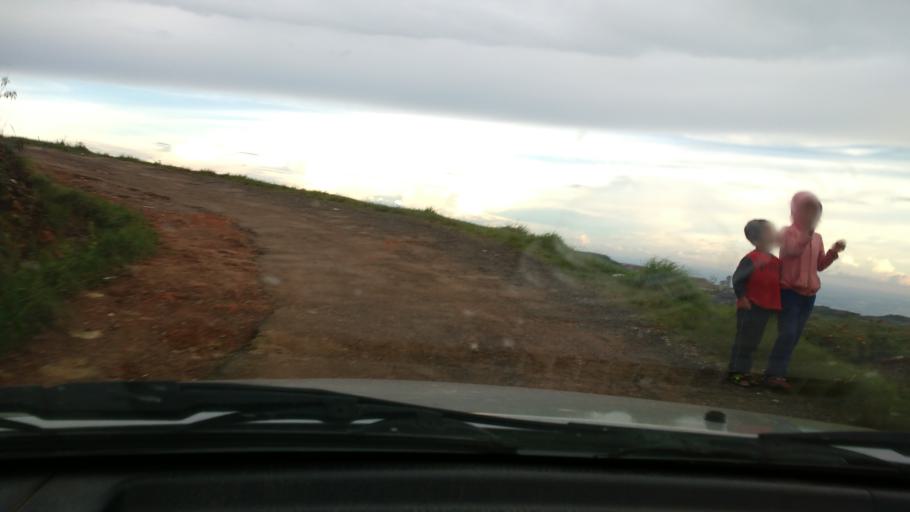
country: IN
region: Meghalaya
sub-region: East Khasi Hills
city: Cherrapunji
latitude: 25.2822
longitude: 91.7108
